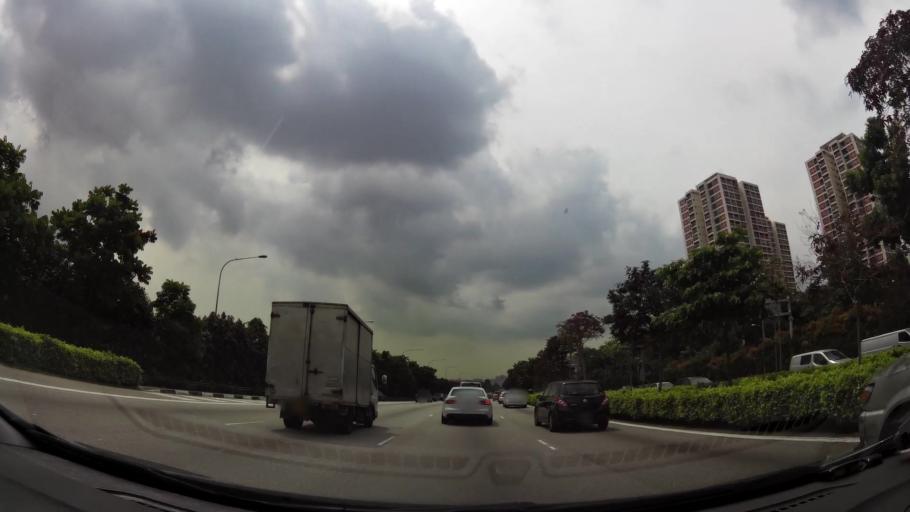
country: SG
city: Singapore
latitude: 1.3673
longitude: 103.8607
